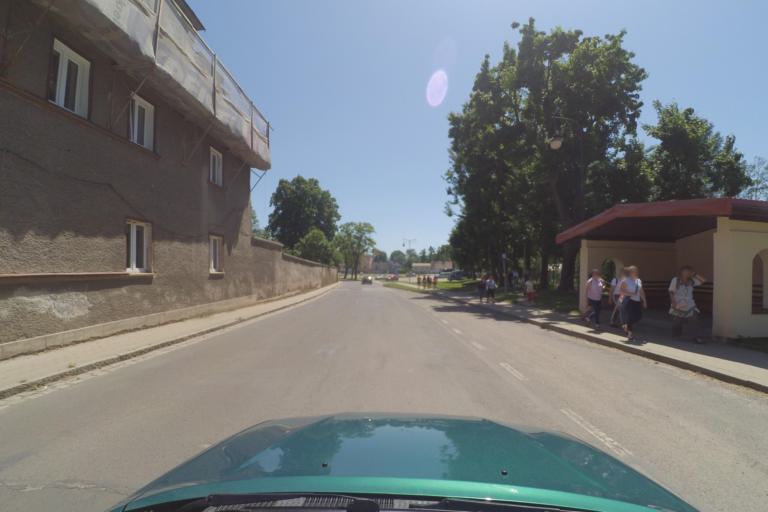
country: PL
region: Lower Silesian Voivodeship
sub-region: Powiat kamiennogorski
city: Krzeszow
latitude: 50.7321
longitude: 16.0670
